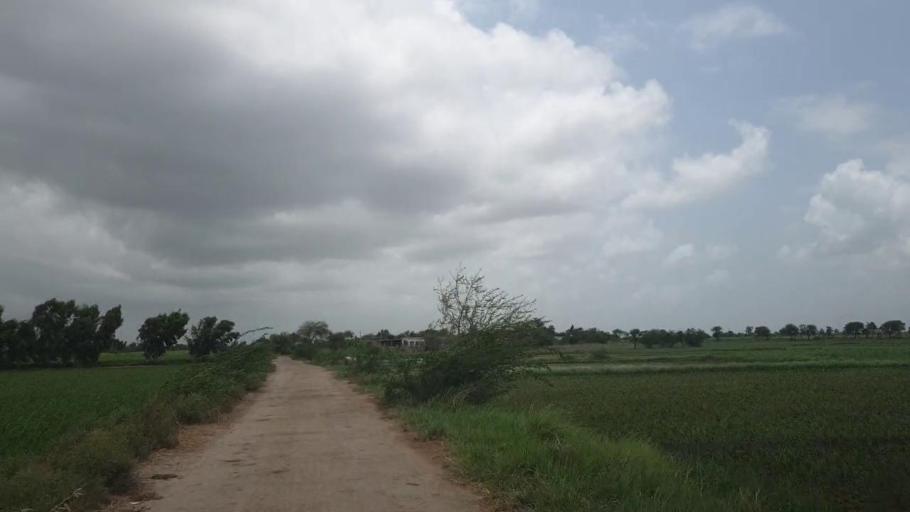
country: PK
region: Sindh
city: Badin
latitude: 24.6680
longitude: 68.9055
